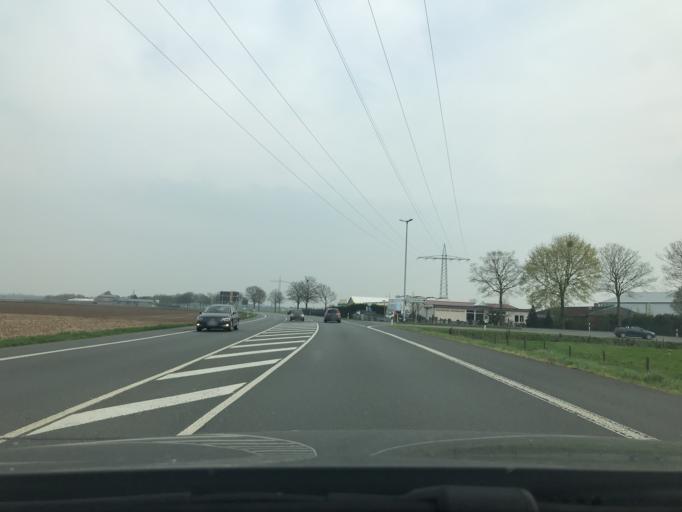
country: DE
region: North Rhine-Westphalia
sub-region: Regierungsbezirk Dusseldorf
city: Wachtendonk
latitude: 51.4514
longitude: 6.3875
